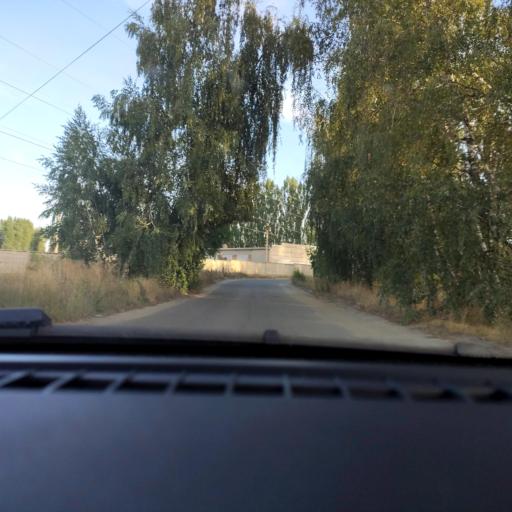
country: RU
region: Voronezj
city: Maslovka
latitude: 51.5784
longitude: 39.2993
